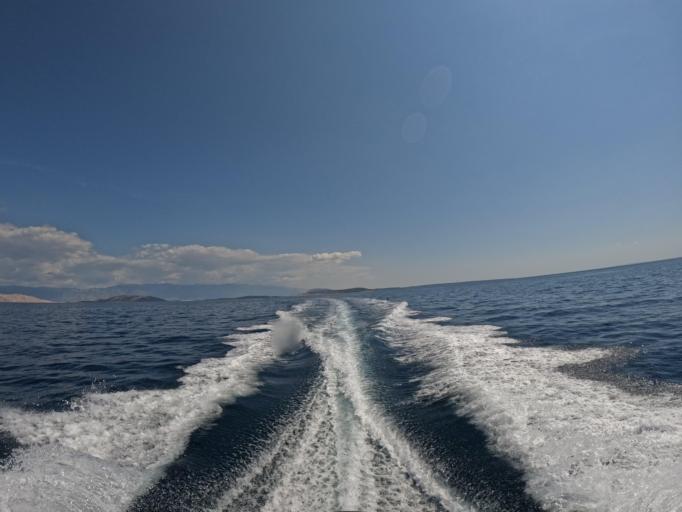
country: HR
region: Primorsko-Goranska
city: Lopar
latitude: 44.8863
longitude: 14.6407
